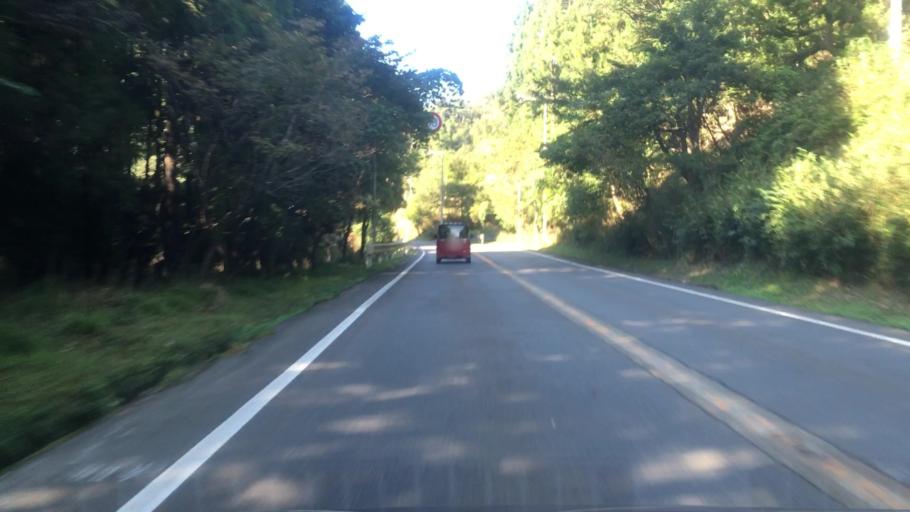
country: JP
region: Hyogo
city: Toyooka
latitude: 35.5652
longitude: 134.8526
